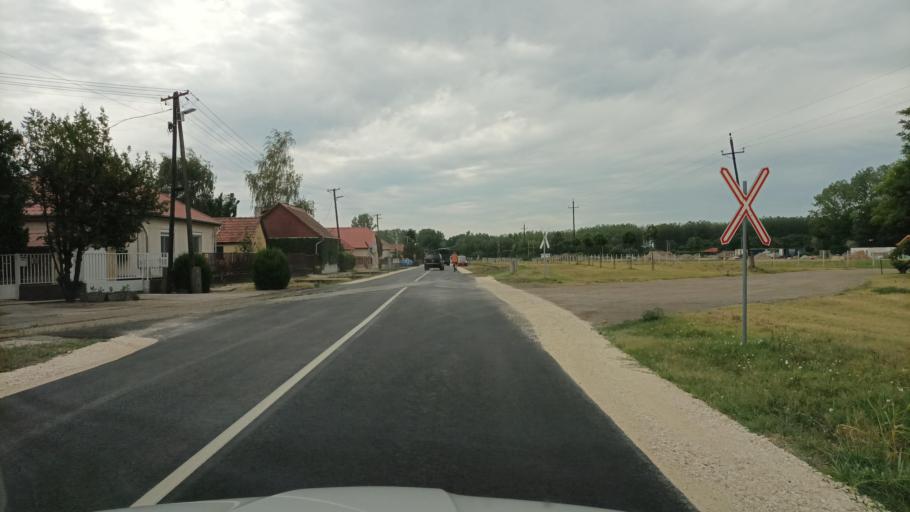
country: HU
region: Pest
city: Taborfalva
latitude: 47.0988
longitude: 19.4766
